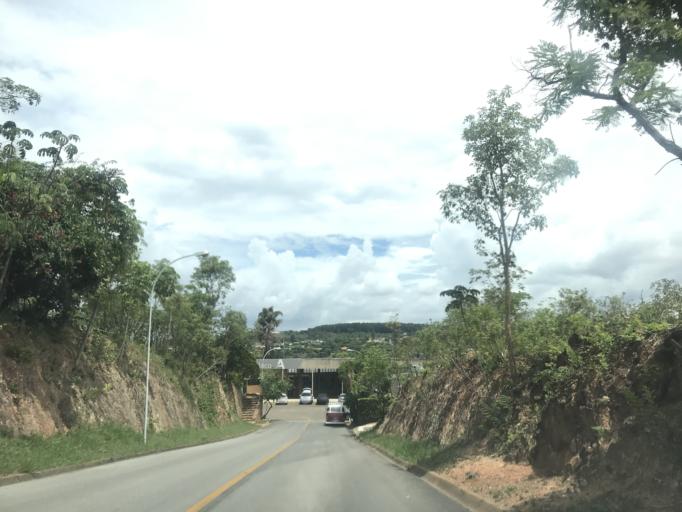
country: BR
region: Federal District
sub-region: Brasilia
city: Brasilia
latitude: -15.7963
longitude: -47.7995
